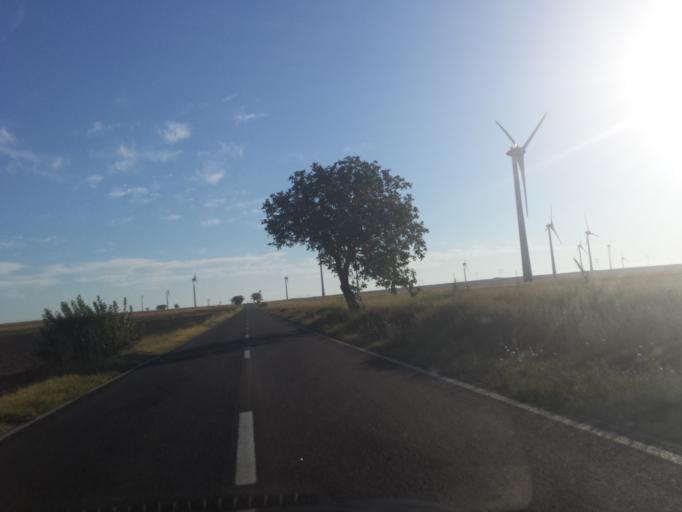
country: RO
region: Constanta
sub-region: Comuna Saraiu
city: Saraiu
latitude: 44.7707
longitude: 28.2174
